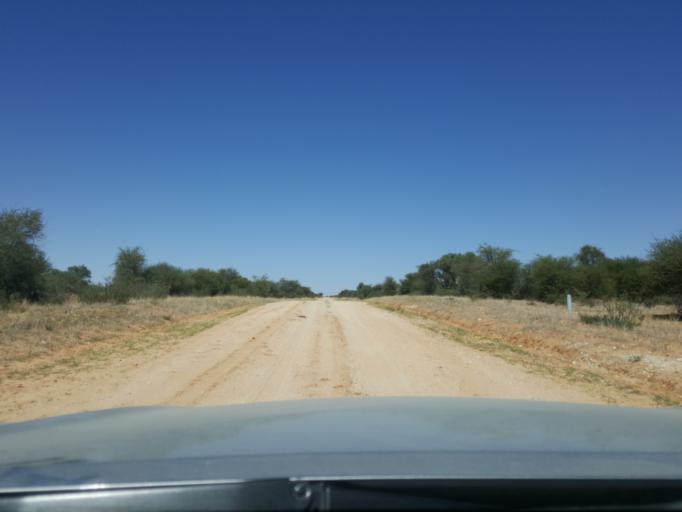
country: BW
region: Kgalagadi
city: Hukuntsi
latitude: -24.0954
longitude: 21.2292
